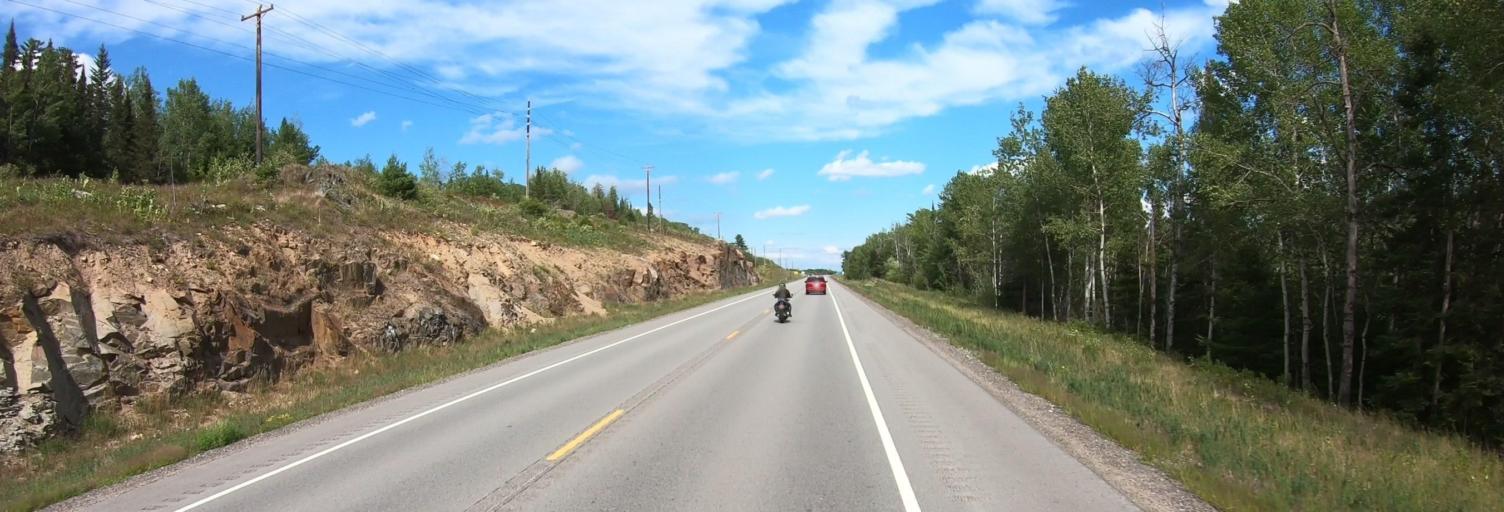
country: US
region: Minnesota
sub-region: Saint Louis County
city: Babbitt
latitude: 47.8494
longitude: -92.0962
